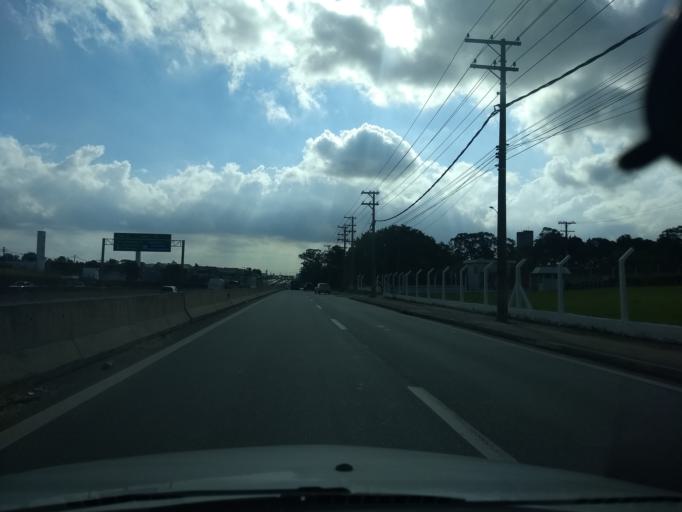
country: BR
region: Sao Paulo
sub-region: Guarulhos
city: Guarulhos
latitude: -23.4441
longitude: -46.4483
